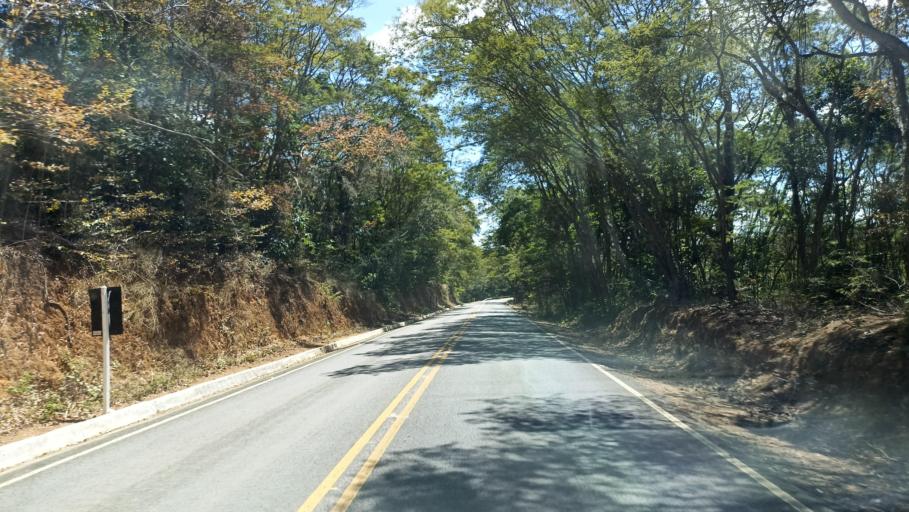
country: BR
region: Bahia
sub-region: Andarai
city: Vera Cruz
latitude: -12.7717
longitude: -41.3306
